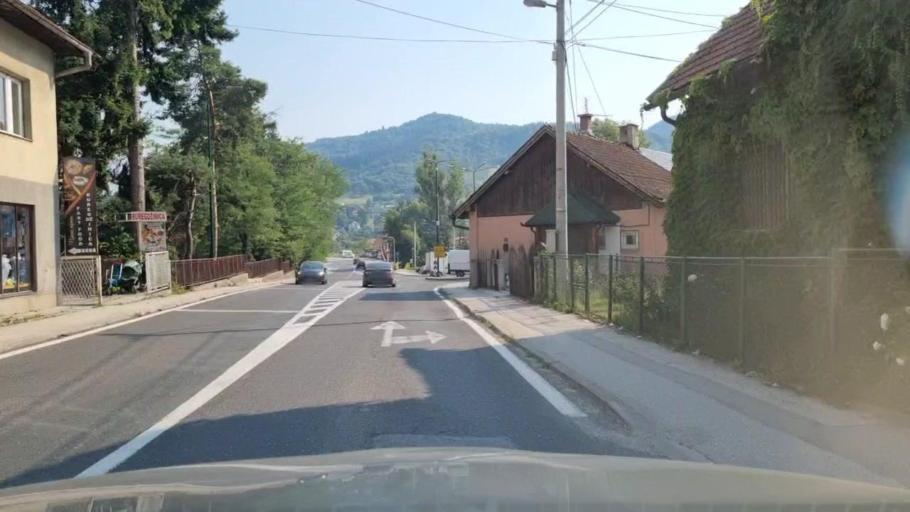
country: BA
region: Federation of Bosnia and Herzegovina
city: Vogosca
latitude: 43.9224
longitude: 18.3173
